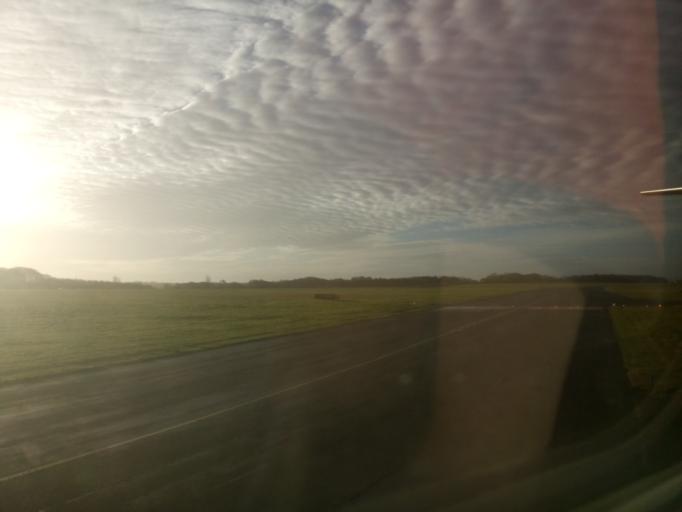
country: GB
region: England
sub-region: Newcastle upon Tyne
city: Dinnington
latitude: 55.0421
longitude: -1.6811
